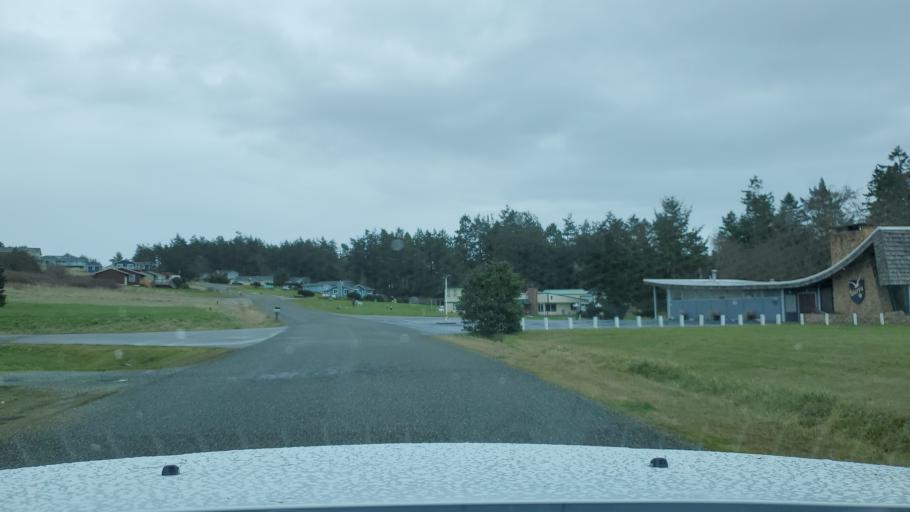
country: US
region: Washington
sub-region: Island County
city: Coupeville
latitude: 48.2335
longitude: -122.7624
